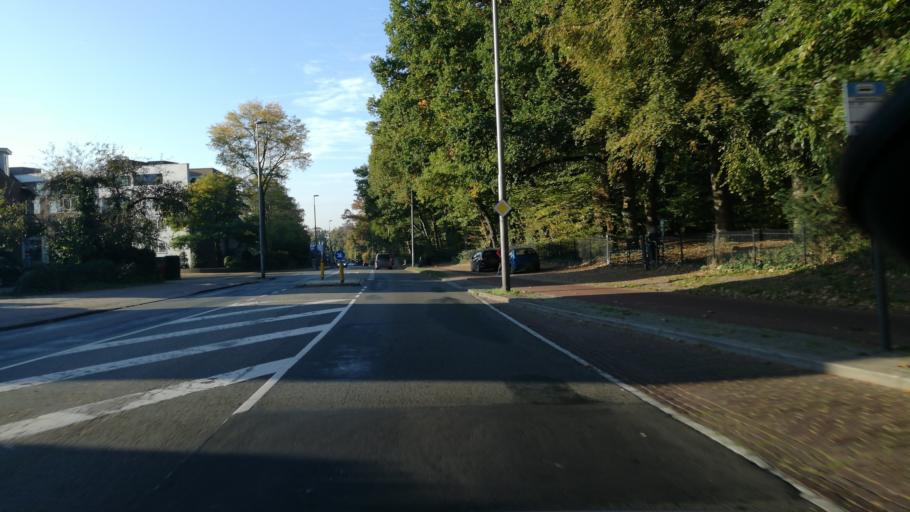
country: NL
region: Gelderland
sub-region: Gemeente Arnhem
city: Arnhem
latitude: 51.9930
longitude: 5.9097
